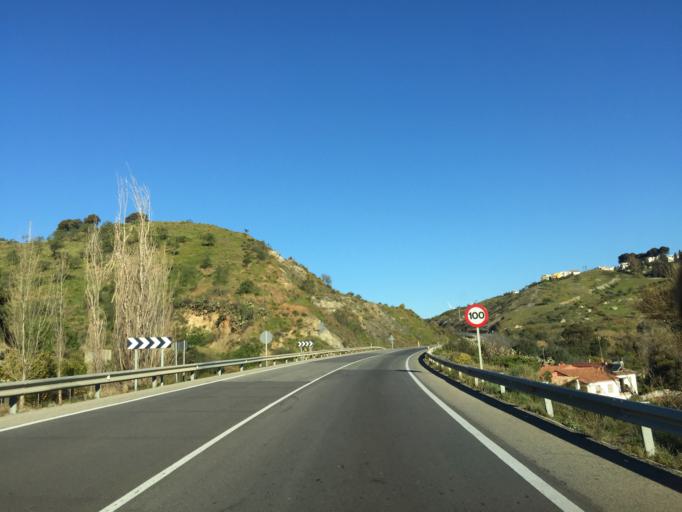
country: ES
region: Andalusia
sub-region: Provincia de Malaga
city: Carratraca
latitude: 36.8430
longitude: -4.8160
